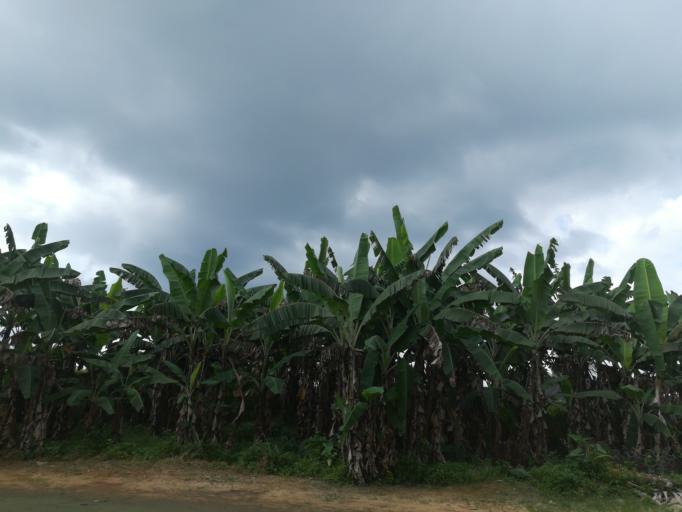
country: NG
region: Rivers
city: Okrika
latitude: 4.7270
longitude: 7.1445
